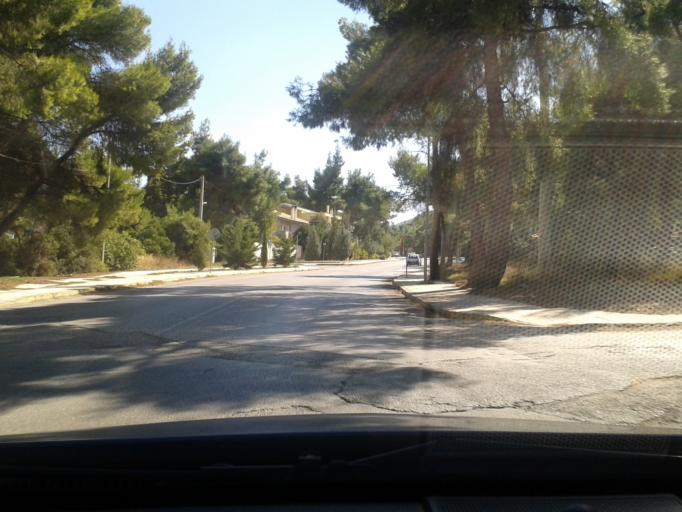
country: GR
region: Attica
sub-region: Nomarchia Anatolikis Attikis
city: Drosia
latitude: 38.1101
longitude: 23.8585
